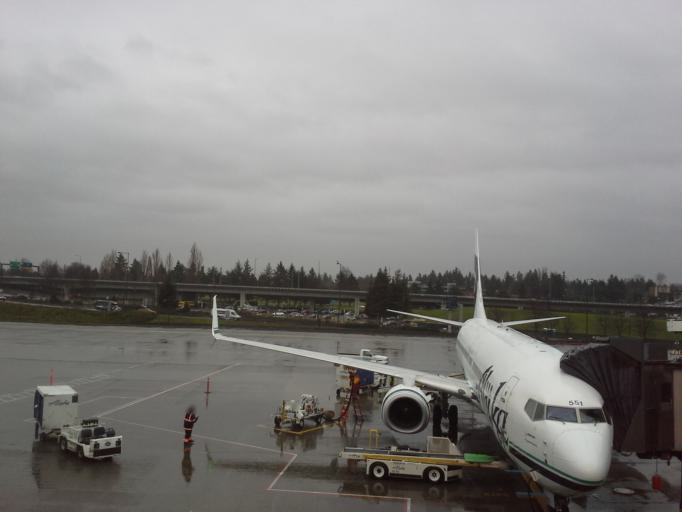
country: US
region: Washington
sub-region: King County
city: SeaTac
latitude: 47.4482
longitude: -122.3010
